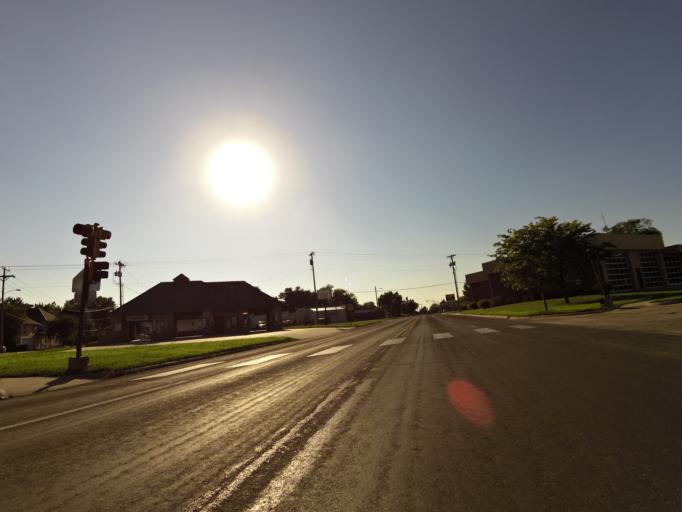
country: US
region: Kansas
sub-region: Harvey County
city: Hesston
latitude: 38.1377
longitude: -97.4302
